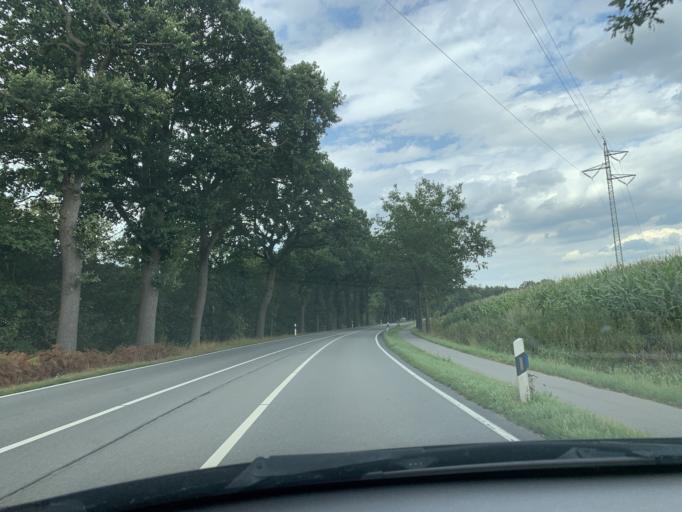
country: DE
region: Lower Saxony
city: Westerstede
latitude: 53.2349
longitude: 7.9057
